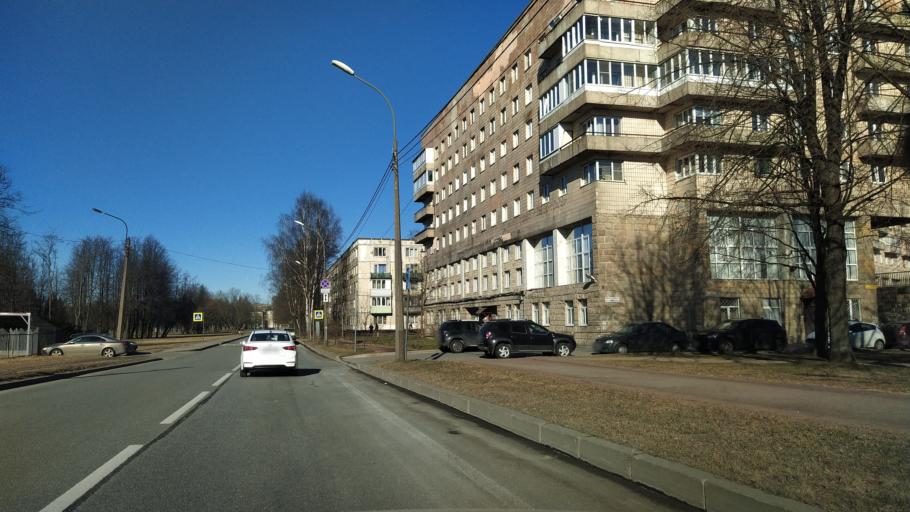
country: RU
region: Leningrad
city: Kalininskiy
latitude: 59.9940
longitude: 30.4279
